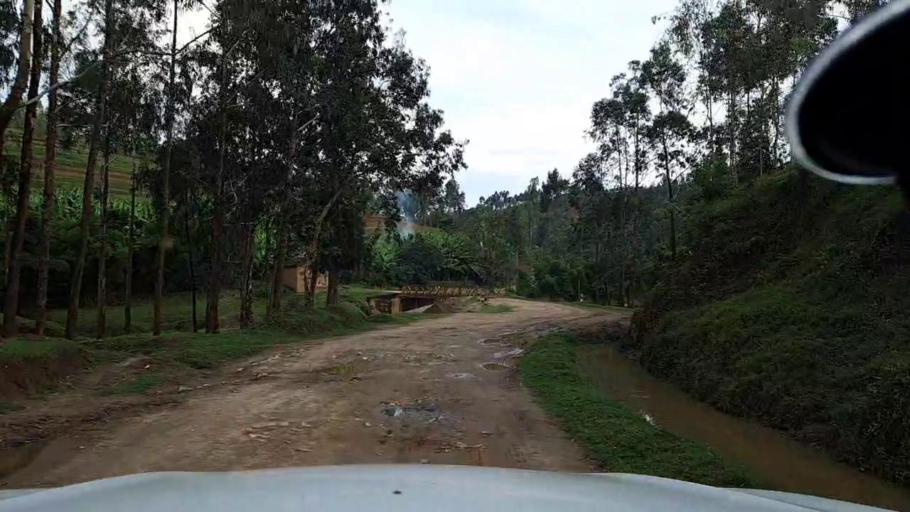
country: RW
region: Western Province
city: Kibuye
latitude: -2.1524
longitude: 29.5384
